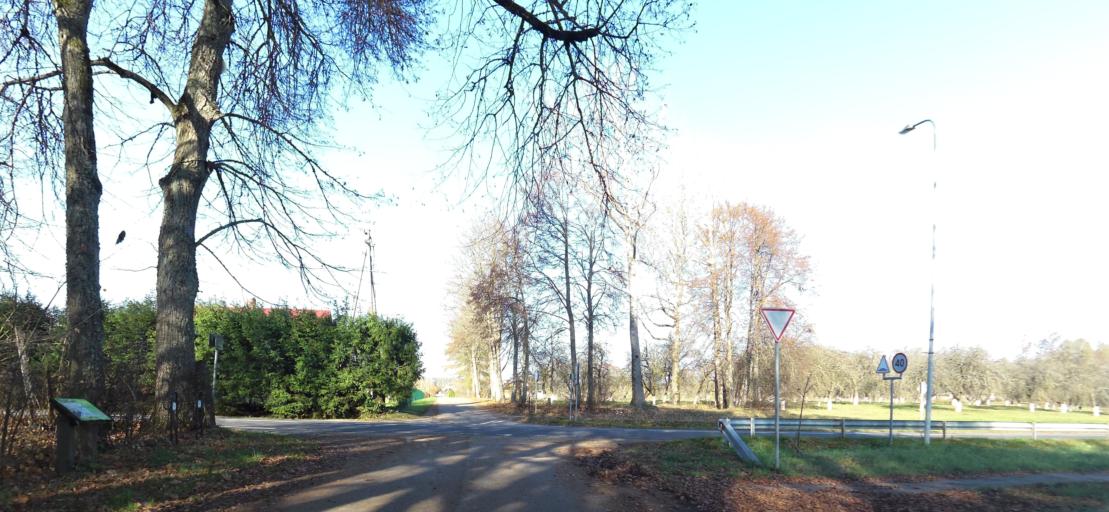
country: LT
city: Aukstadvaris
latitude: 54.5771
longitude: 24.5198
